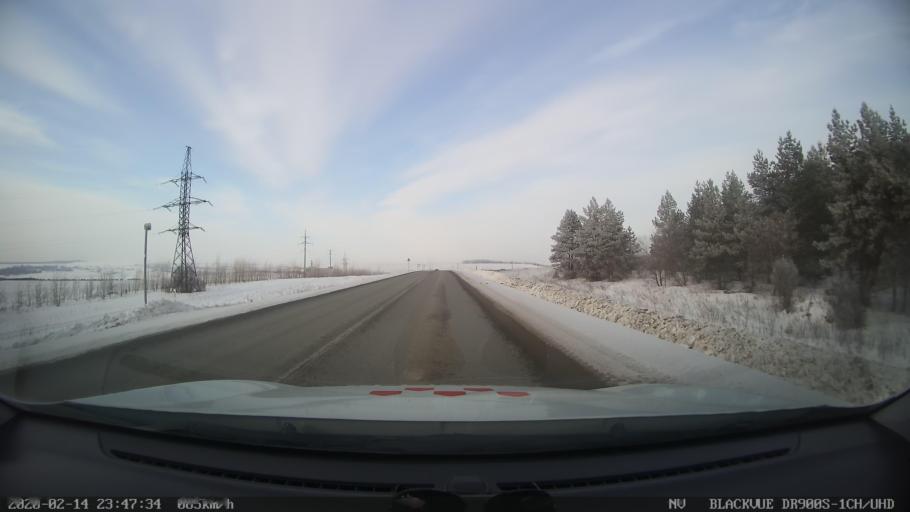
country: RU
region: Tatarstan
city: Kuybyshevskiy Zaton
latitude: 55.2399
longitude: 49.2081
